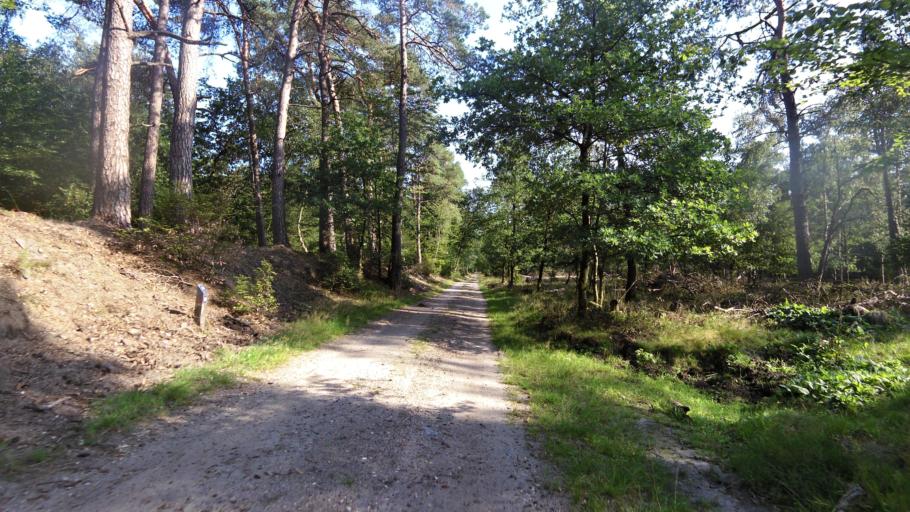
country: NL
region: Gelderland
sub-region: Gemeente Apeldoorn
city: Loenen
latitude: 52.1130
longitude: 5.9809
